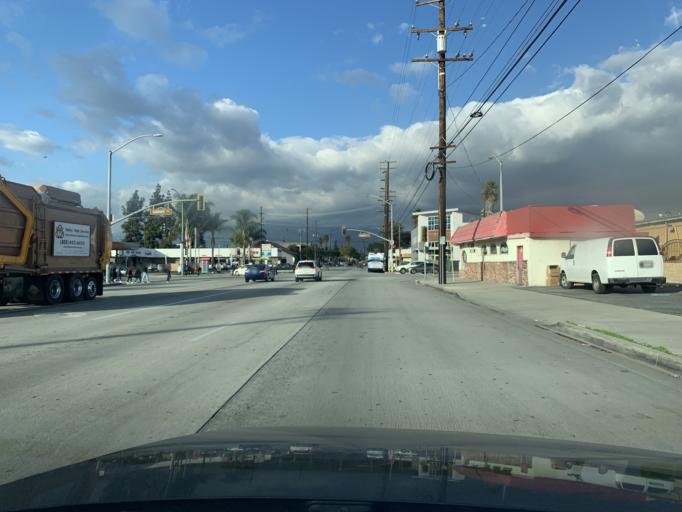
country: US
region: California
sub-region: Los Angeles County
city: El Monte
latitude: 34.0623
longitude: -118.0304
